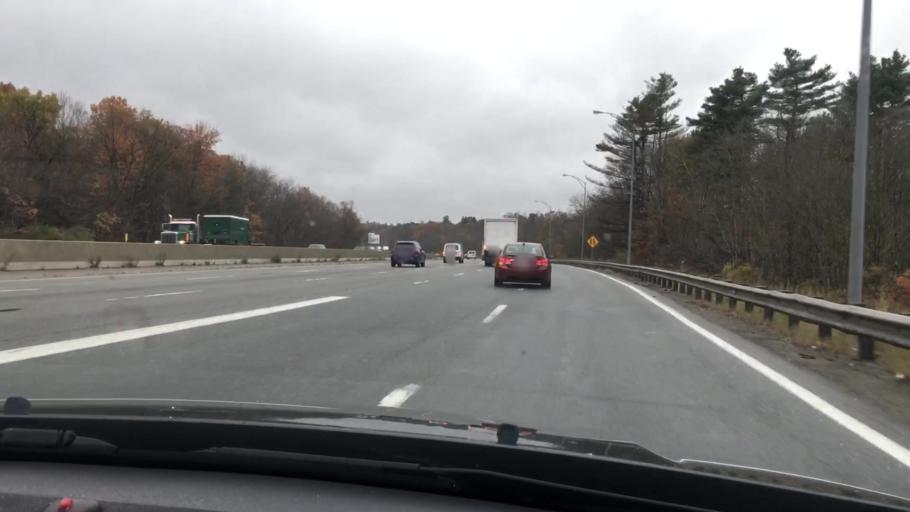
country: US
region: Massachusetts
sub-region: Worcester County
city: Westborough
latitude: 42.2627
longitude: -71.5738
